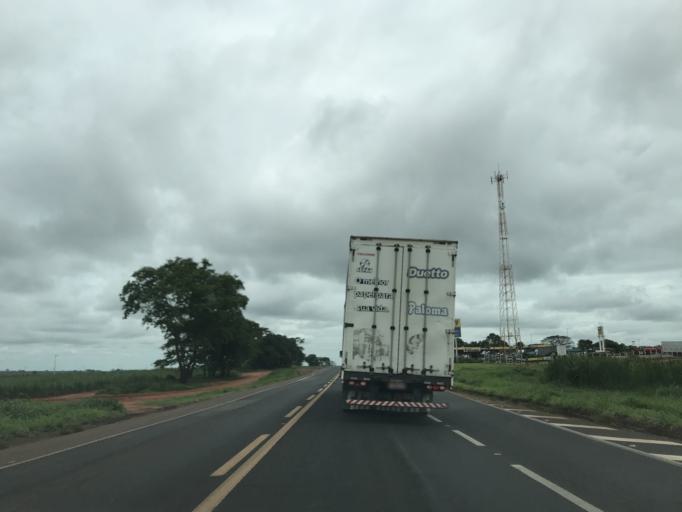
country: BR
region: Sao Paulo
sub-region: Nova Granada
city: Nova Granada
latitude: -20.4504
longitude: -49.2840
